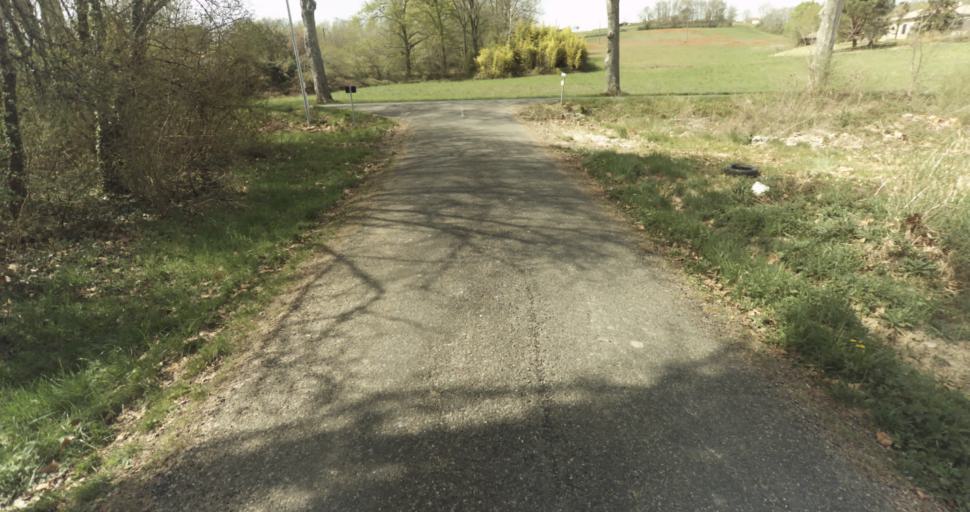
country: FR
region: Midi-Pyrenees
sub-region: Departement du Tarn-et-Garonne
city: Moissac
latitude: 44.1610
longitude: 1.1151
